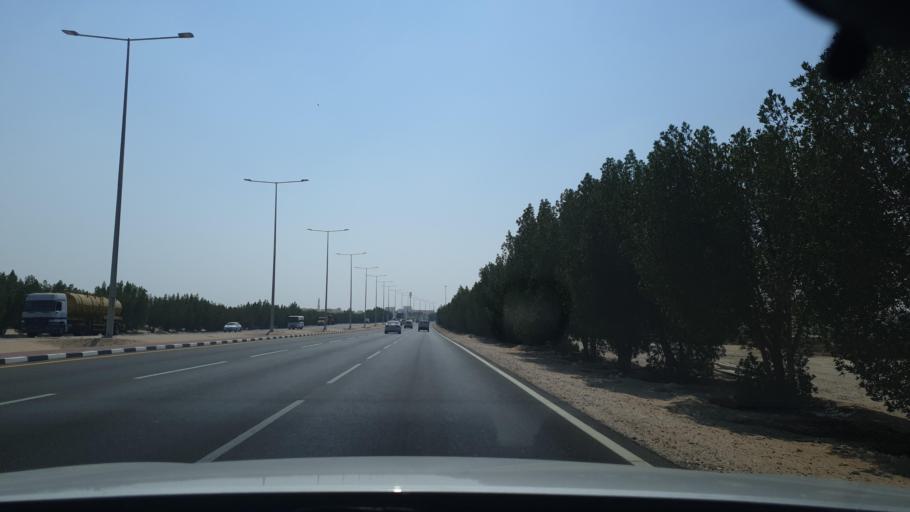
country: QA
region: Al Khawr
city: Al Khawr
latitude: 25.6959
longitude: 51.5016
